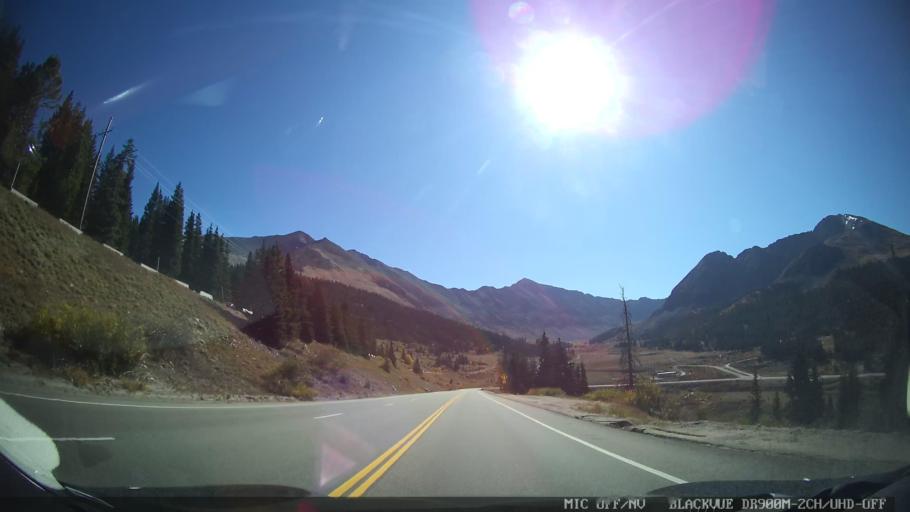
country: US
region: Colorado
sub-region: Lake County
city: Leadville
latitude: 39.3650
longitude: -106.1838
